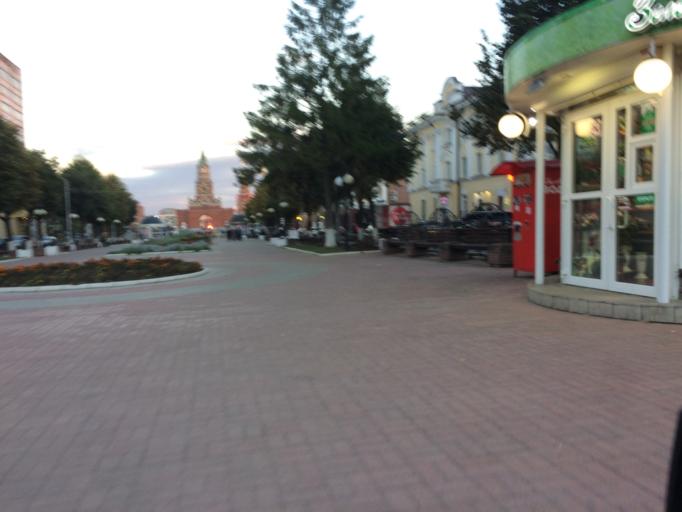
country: RU
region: Mariy-El
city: Yoshkar-Ola
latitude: 56.6348
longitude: 47.8975
